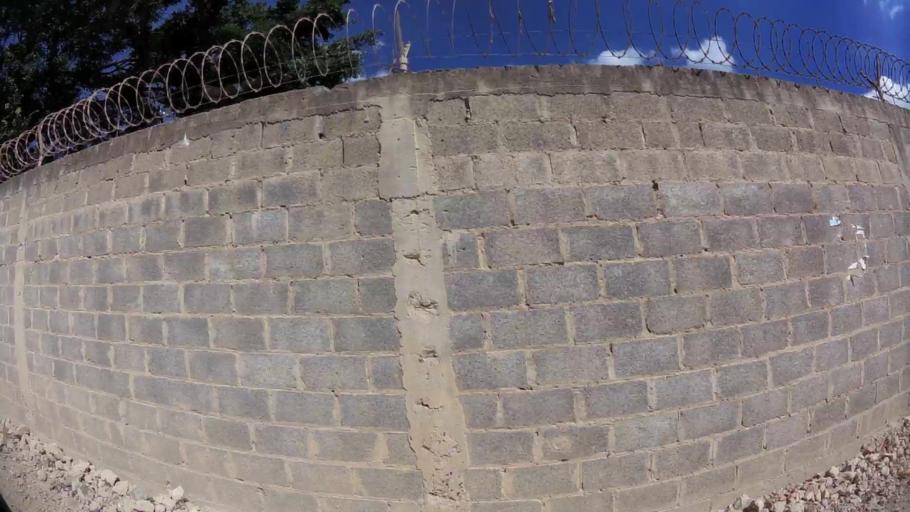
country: DO
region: Santo Domingo
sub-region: Santo Domingo
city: Santo Domingo Este
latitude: 18.4680
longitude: -69.7673
